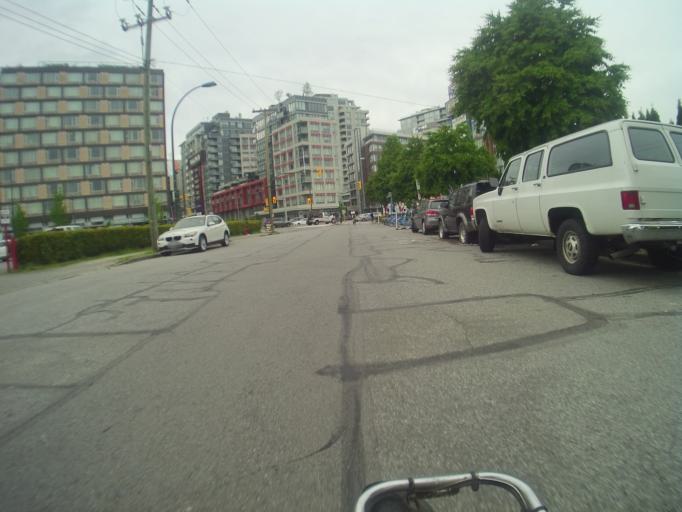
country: CA
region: British Columbia
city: Vancouver
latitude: 49.2698
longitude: -123.0999
